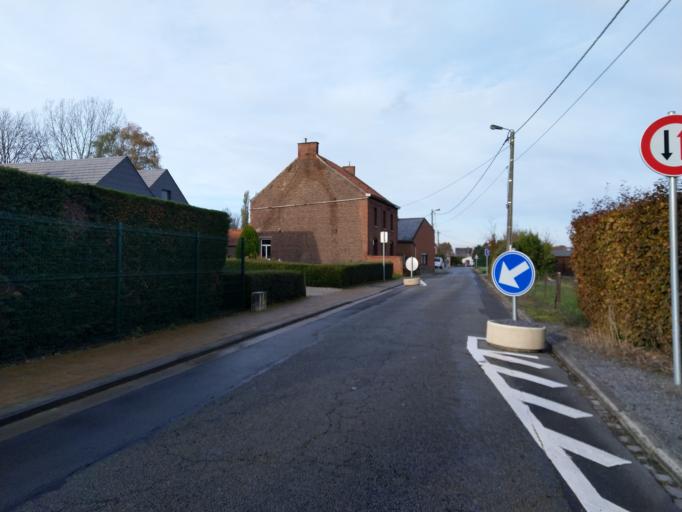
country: BE
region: Wallonia
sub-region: Province du Hainaut
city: Jurbise
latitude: 50.5090
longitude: 3.8615
